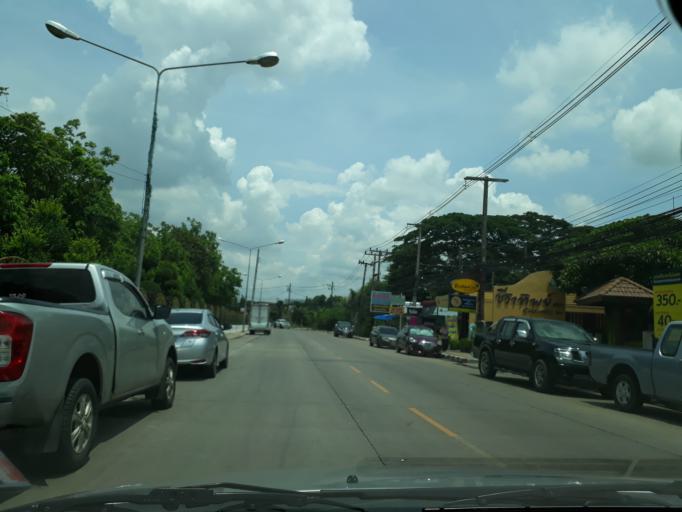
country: TH
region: Khon Kaen
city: Khon Kaen
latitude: 16.4080
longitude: 102.8358
